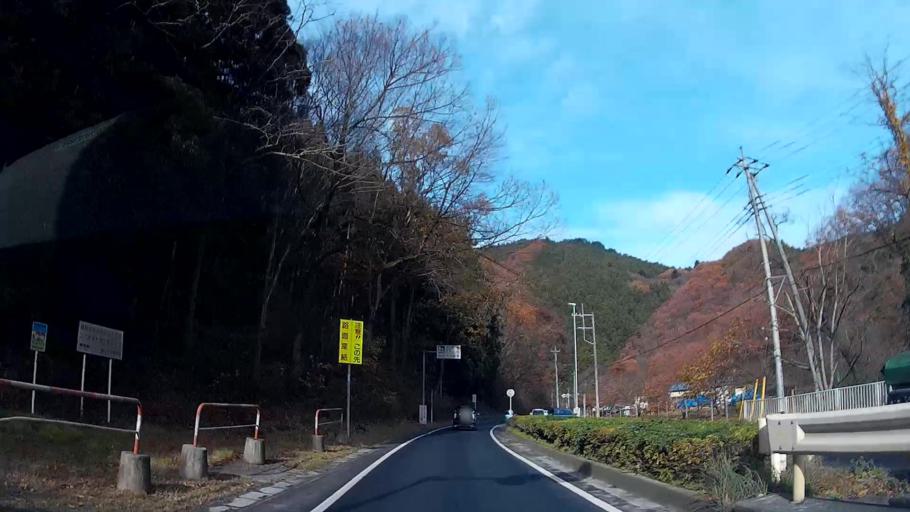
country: JP
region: Saitama
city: Chichibu
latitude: 35.9775
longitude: 139.1278
